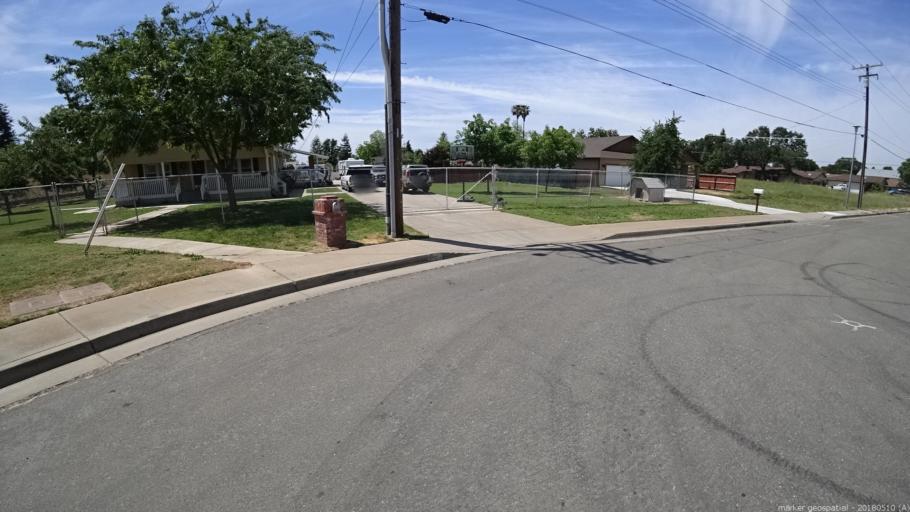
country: US
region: California
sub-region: Sacramento County
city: Sacramento
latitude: 38.6261
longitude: -121.4480
